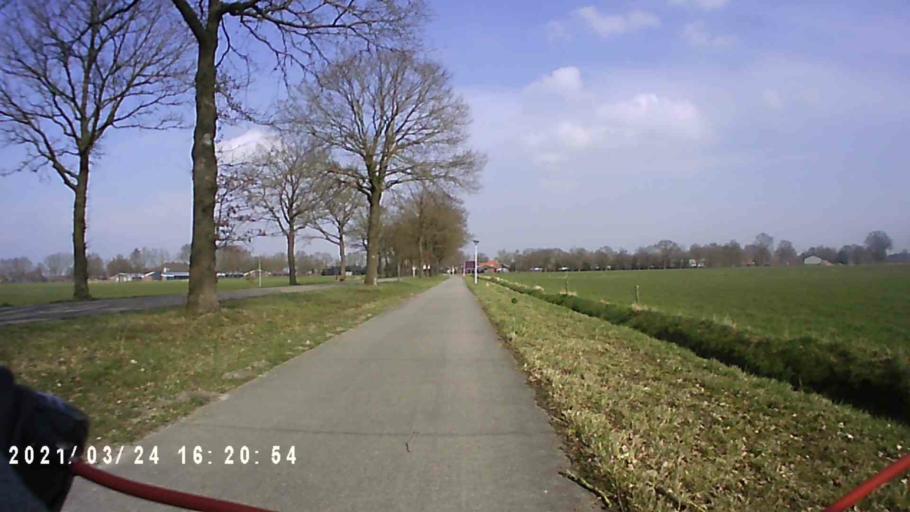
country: NL
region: Friesland
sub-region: Gemeente Smallingerland
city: Drachtstercompagnie
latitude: 53.0542
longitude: 6.2690
